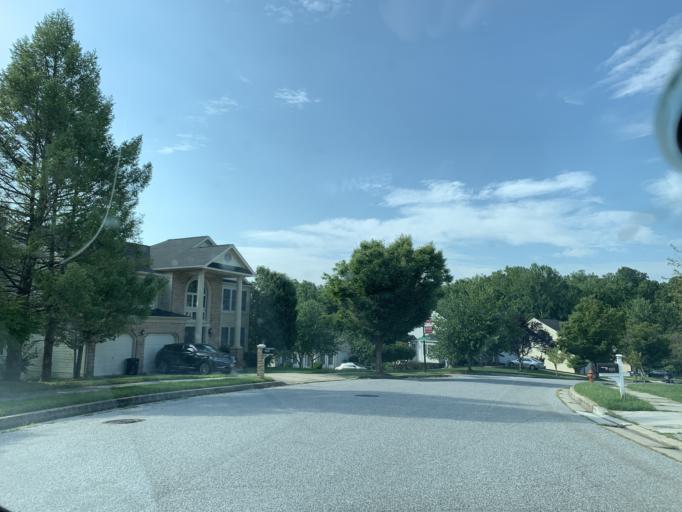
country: US
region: Maryland
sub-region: Baltimore County
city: Randallstown
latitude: 39.3912
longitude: -76.7949
